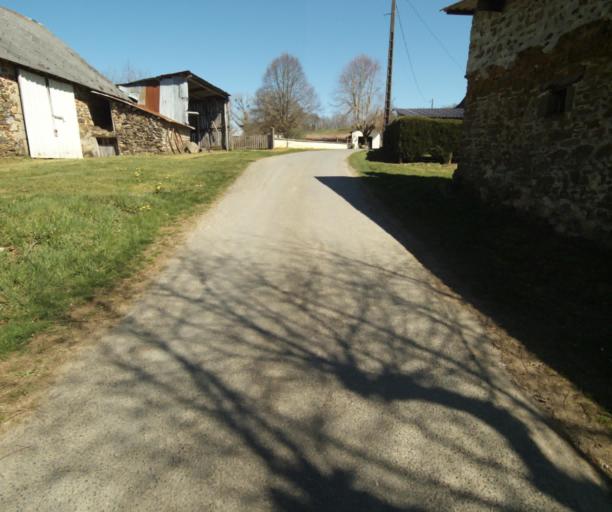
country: FR
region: Limousin
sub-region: Departement de la Correze
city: Chamboulive
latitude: 45.4471
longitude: 1.6737
